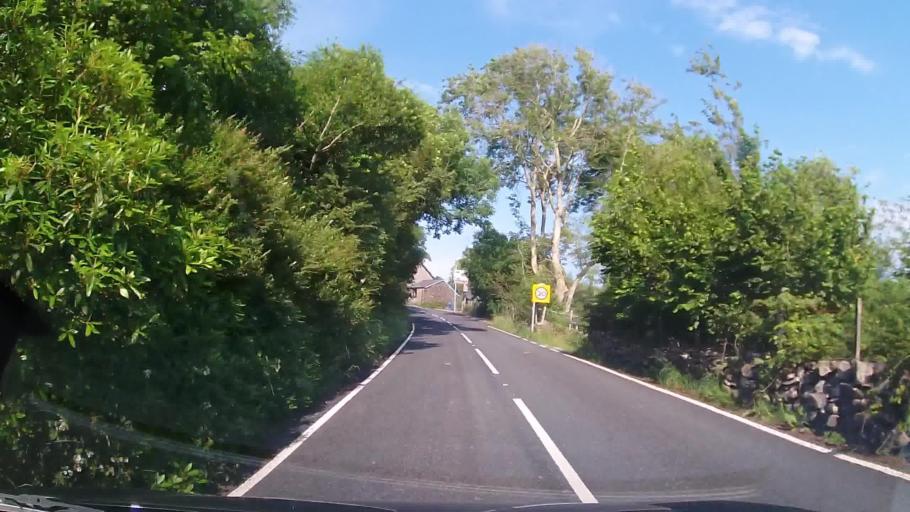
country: GB
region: Wales
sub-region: Gwynedd
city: Ffestiniog
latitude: 52.9581
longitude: -3.9384
